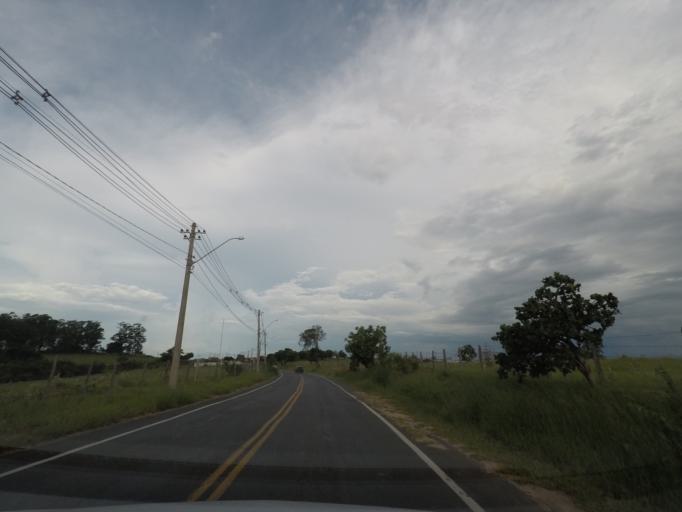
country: BR
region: Sao Paulo
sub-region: Hortolandia
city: Hortolandia
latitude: -22.9580
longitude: -47.2066
